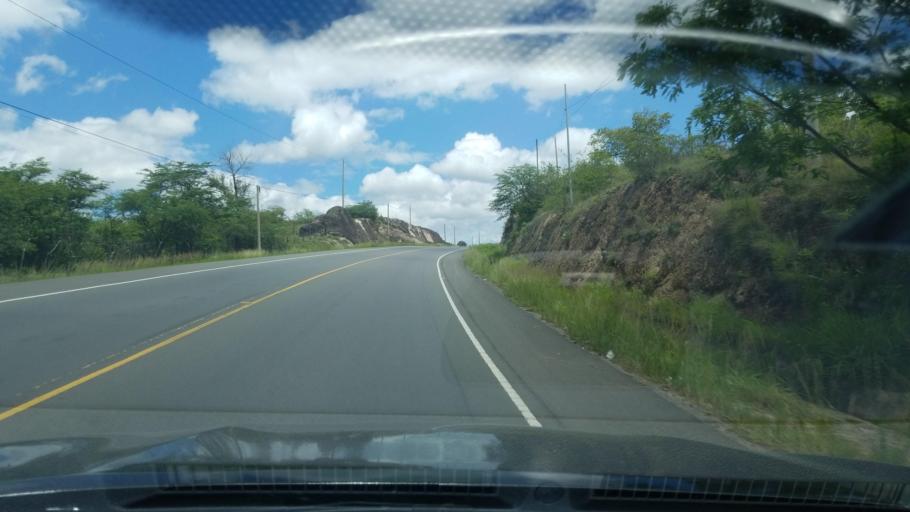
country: HN
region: Francisco Morazan
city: Cofradia
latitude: 14.3075
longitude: -87.2196
